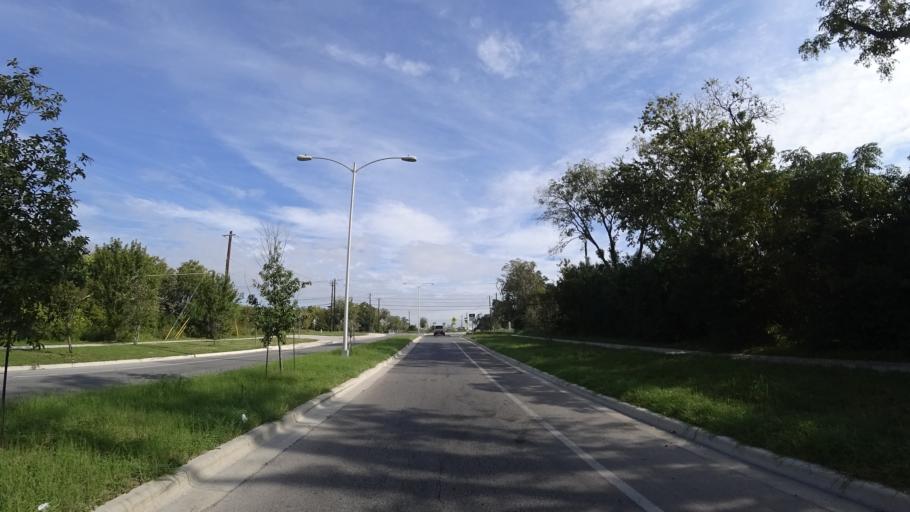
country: US
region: Texas
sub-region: Travis County
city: Austin
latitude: 30.2061
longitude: -97.7409
